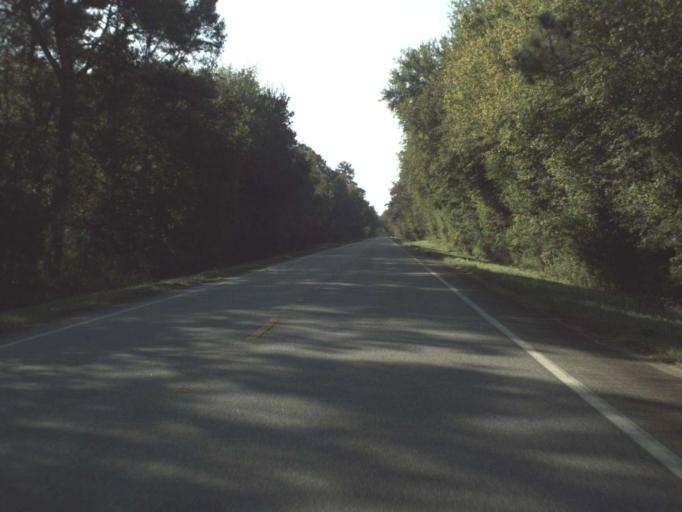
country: US
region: Georgia
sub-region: Brooks County
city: Quitman
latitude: 30.5963
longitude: -83.6425
